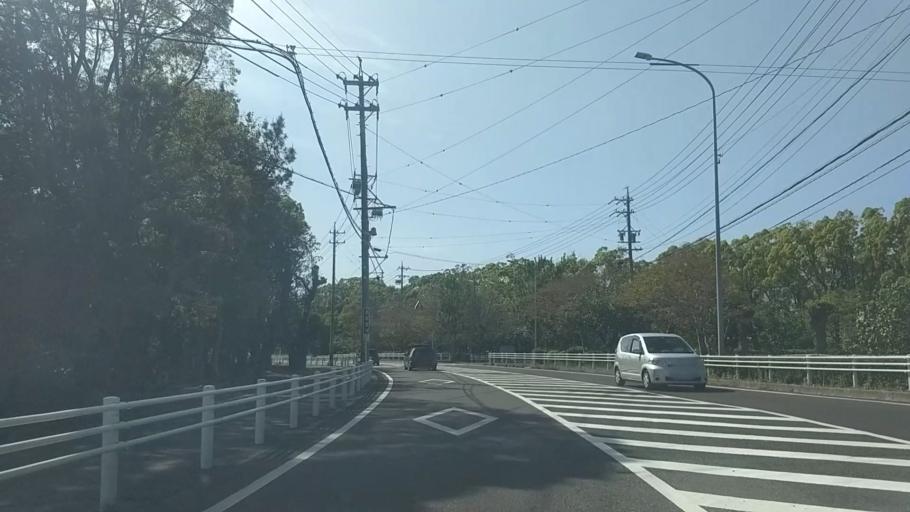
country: JP
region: Aichi
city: Anjo
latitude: 34.9671
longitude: 137.0800
